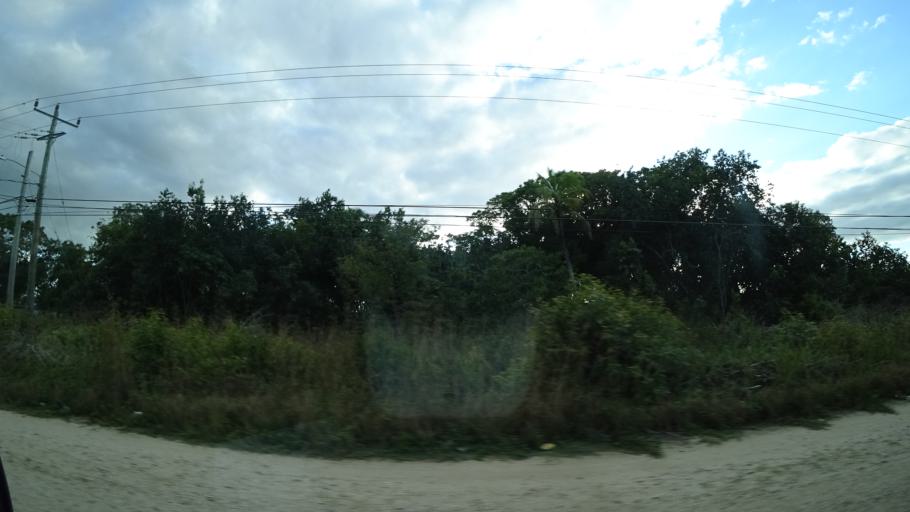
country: BZ
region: Belize
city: Belize City
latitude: 17.5733
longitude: -88.3362
